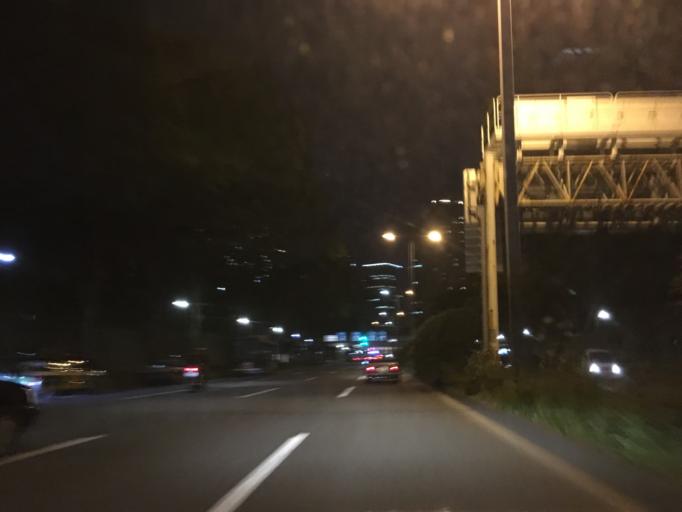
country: JP
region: Tokyo
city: Tokyo
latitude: 35.6871
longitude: 139.6914
